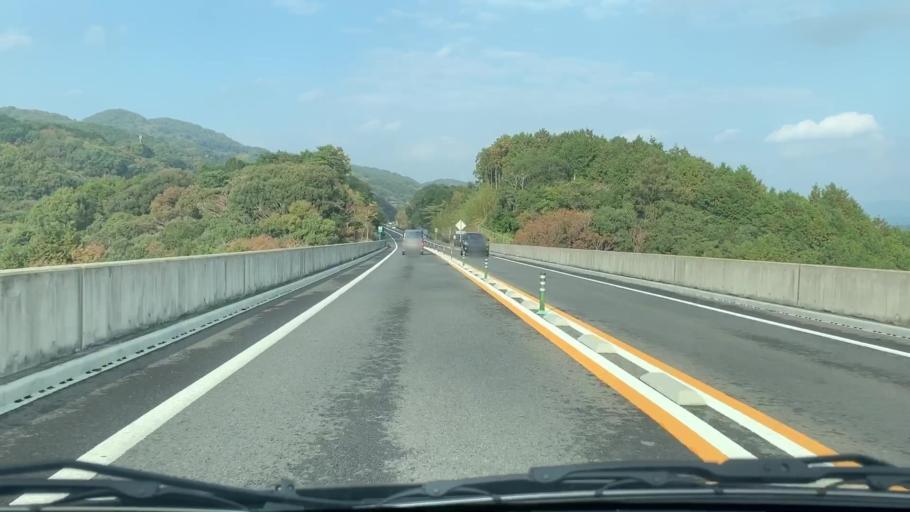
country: JP
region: Nagasaki
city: Sasebo
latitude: 33.0118
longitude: 129.7298
